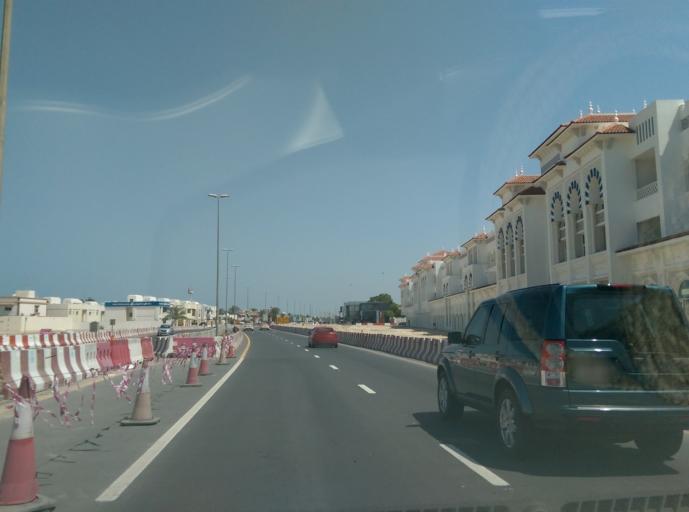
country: AE
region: Dubai
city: Dubai
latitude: 25.1940
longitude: 55.2452
